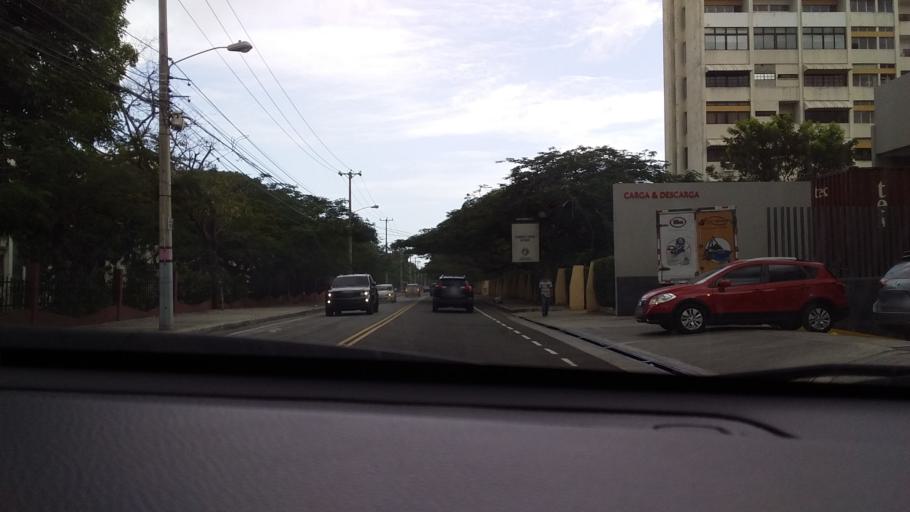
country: DO
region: Nacional
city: Bella Vista
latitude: 18.4561
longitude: -69.9368
